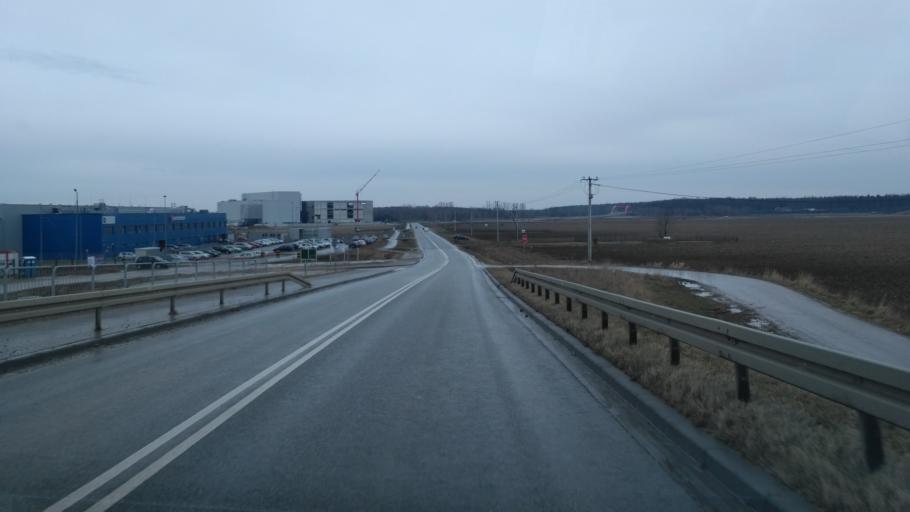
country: PL
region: Subcarpathian Voivodeship
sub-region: Powiat debicki
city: Brzeznica
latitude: 50.0673
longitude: 21.4736
